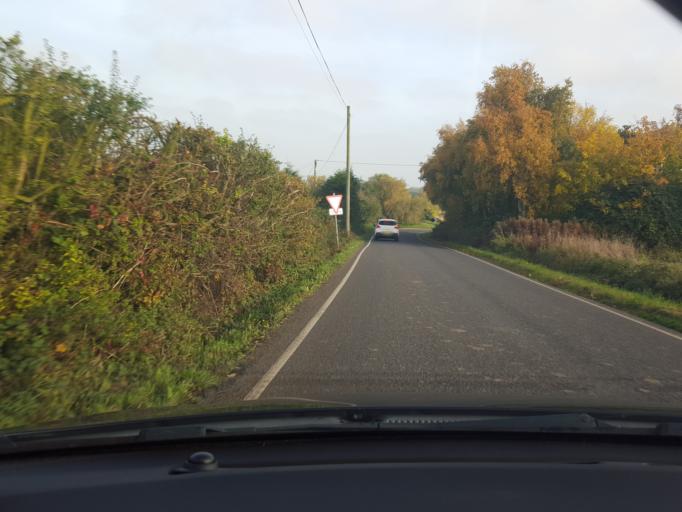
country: GB
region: England
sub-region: Essex
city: Frinton-on-Sea
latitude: 51.8570
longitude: 1.2065
